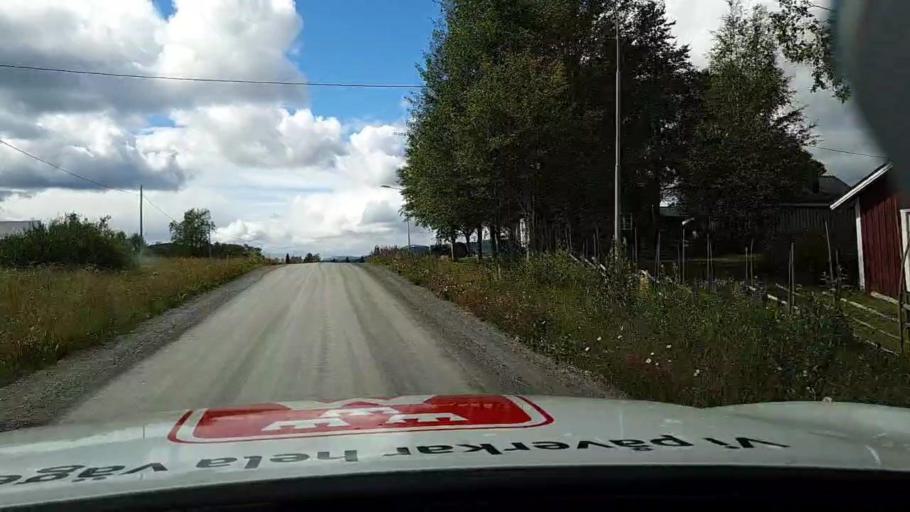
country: SE
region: Jaemtland
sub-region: Krokoms Kommun
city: Valla
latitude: 63.6991
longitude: 13.6050
